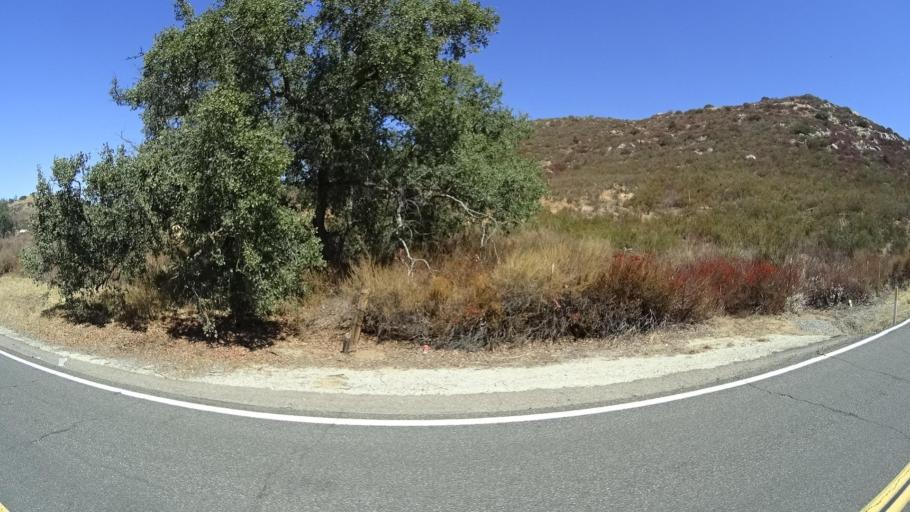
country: US
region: California
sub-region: San Diego County
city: San Diego Country Estates
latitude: 33.0580
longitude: -116.7678
